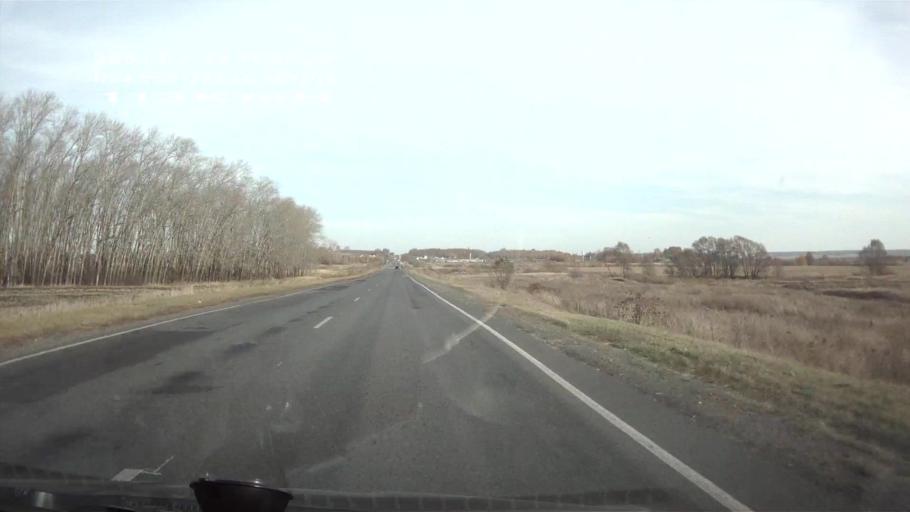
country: RU
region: Mordoviya
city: Atyashevo
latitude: 54.5531
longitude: 45.9610
